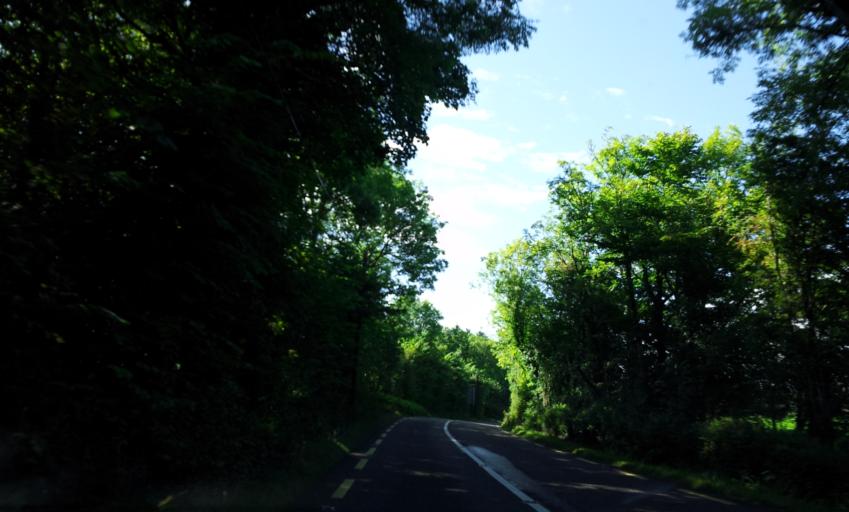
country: IE
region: Munster
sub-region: County Cork
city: Millstreet
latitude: 51.9467
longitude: -9.1760
